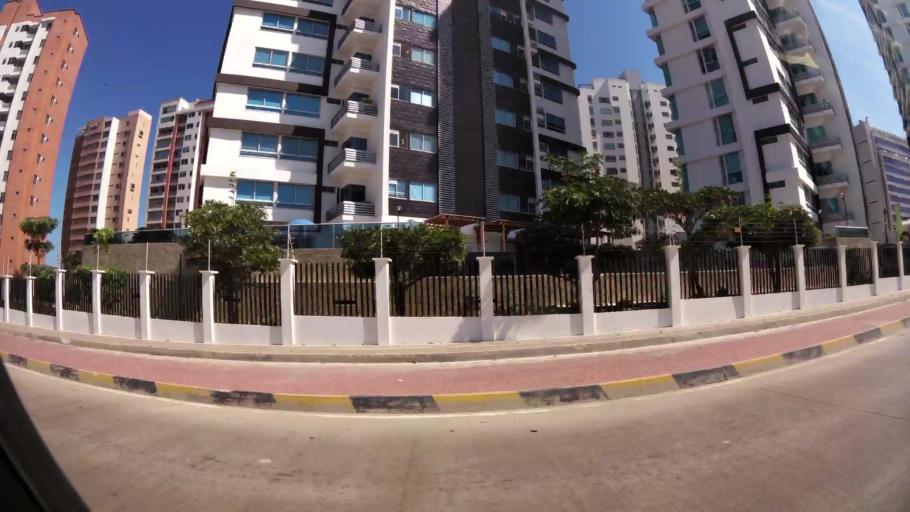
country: CO
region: Atlantico
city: Barranquilla
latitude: 11.0170
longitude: -74.8333
